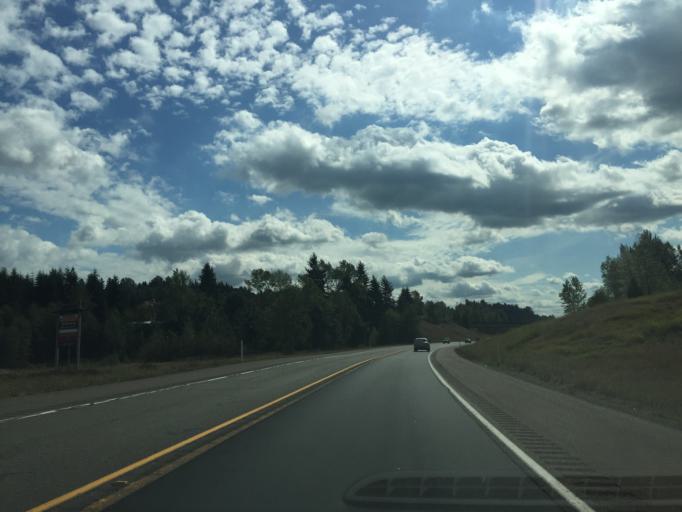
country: US
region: Washington
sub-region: Snohomish County
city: Snohomish
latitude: 47.9387
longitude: -122.0700
